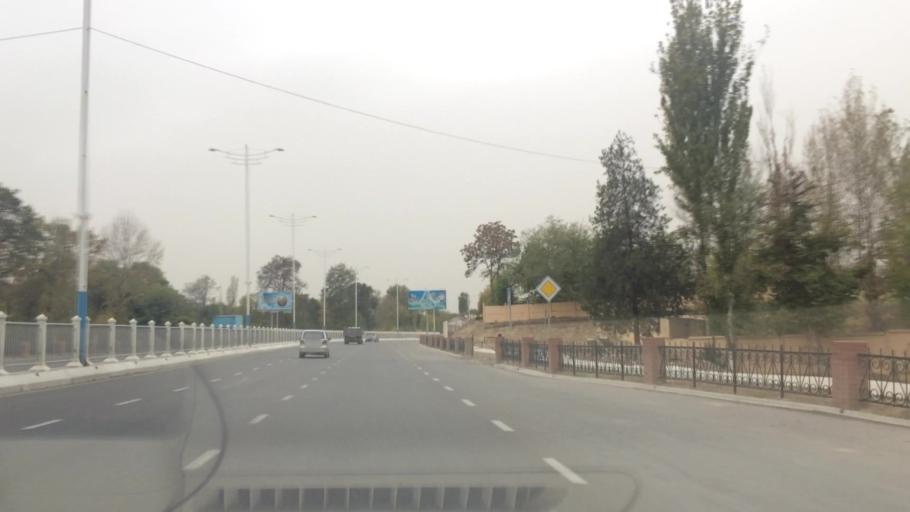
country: UZ
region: Toshkent
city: Salor
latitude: 41.3039
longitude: 69.3186
